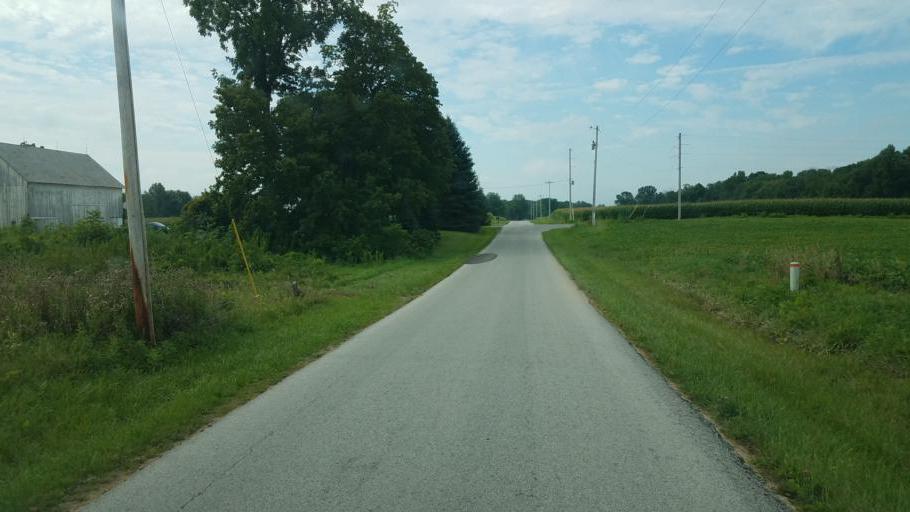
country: US
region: Ohio
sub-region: Morrow County
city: Cardington
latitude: 40.5001
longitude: -82.9488
